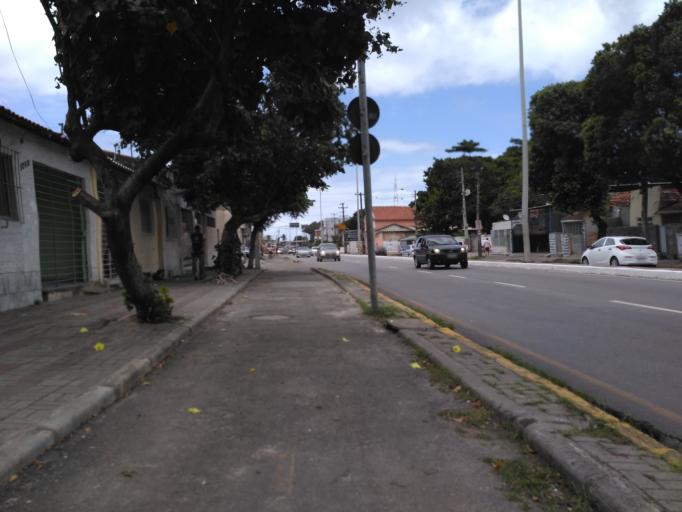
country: BR
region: Pernambuco
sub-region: Recife
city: Recife
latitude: -8.0434
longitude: -34.8835
